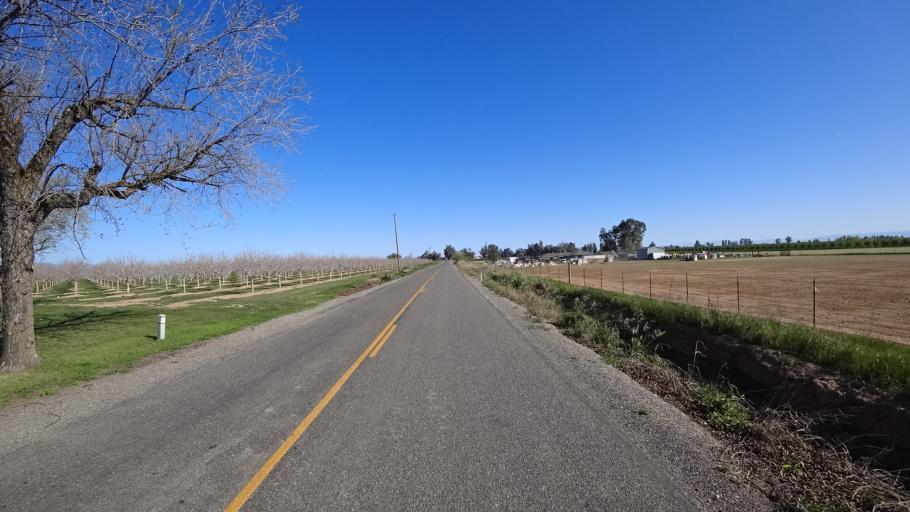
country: US
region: California
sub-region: Glenn County
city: Orland
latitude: 39.7484
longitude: -122.2481
